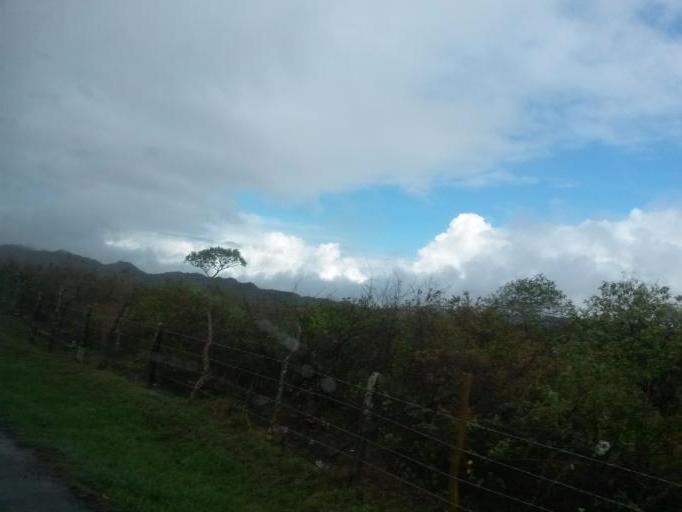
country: CO
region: Cauca
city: El Bordo
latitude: 2.1481
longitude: -76.9239
